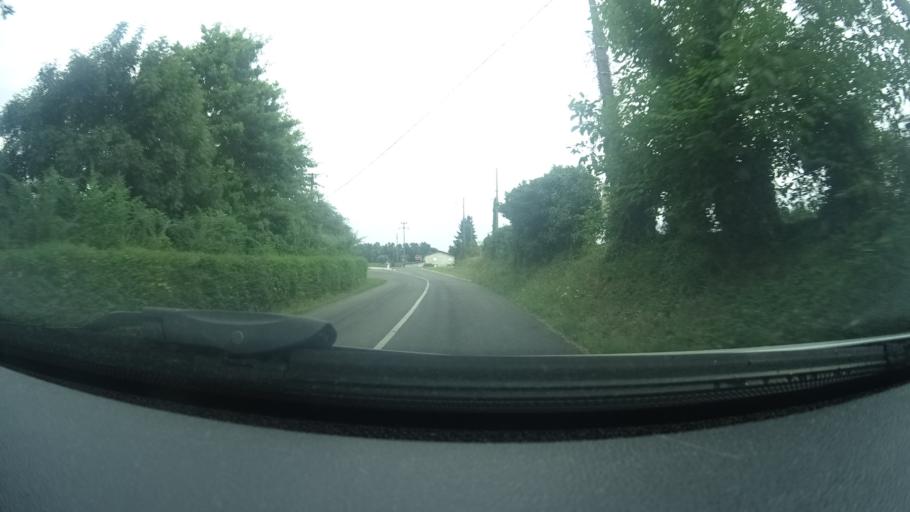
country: FR
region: Aquitaine
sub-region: Departement des Pyrenees-Atlantiques
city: Mont
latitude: 43.4479
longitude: -0.6896
